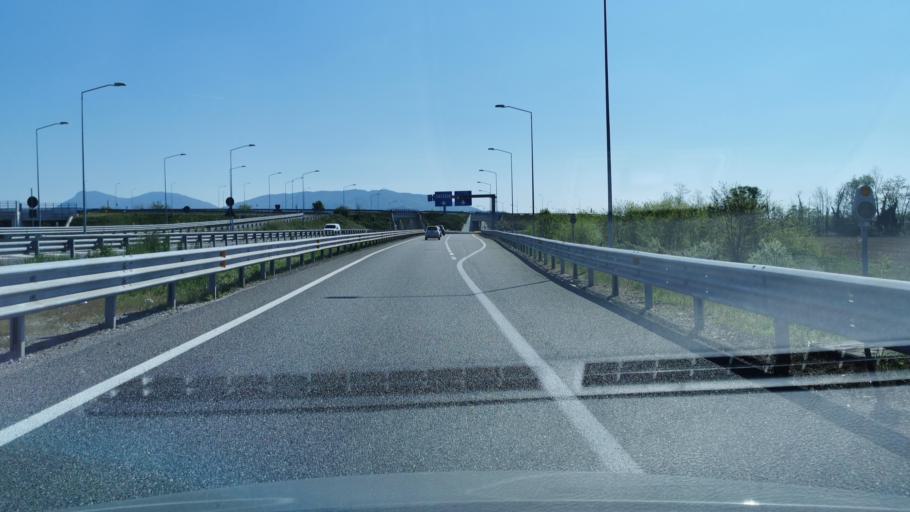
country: IT
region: Lombardy
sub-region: Provincia di Brescia
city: Castegnato
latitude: 45.5481
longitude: 10.1286
